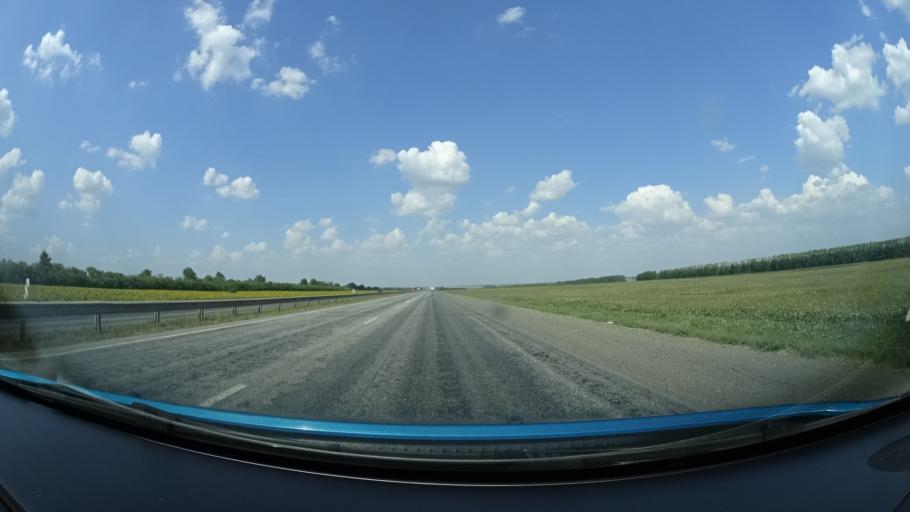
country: RU
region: Bashkortostan
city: Dmitriyevka
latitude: 54.7059
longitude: 55.2363
